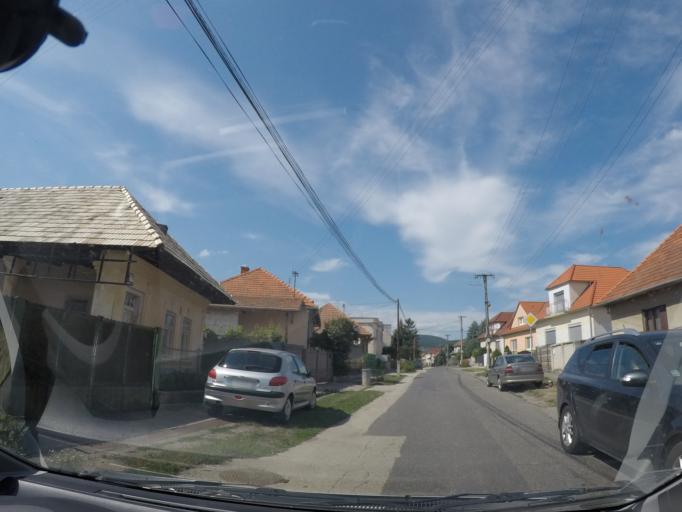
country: SK
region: Nitriansky
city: Tlmace
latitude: 48.2889
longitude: 18.6025
